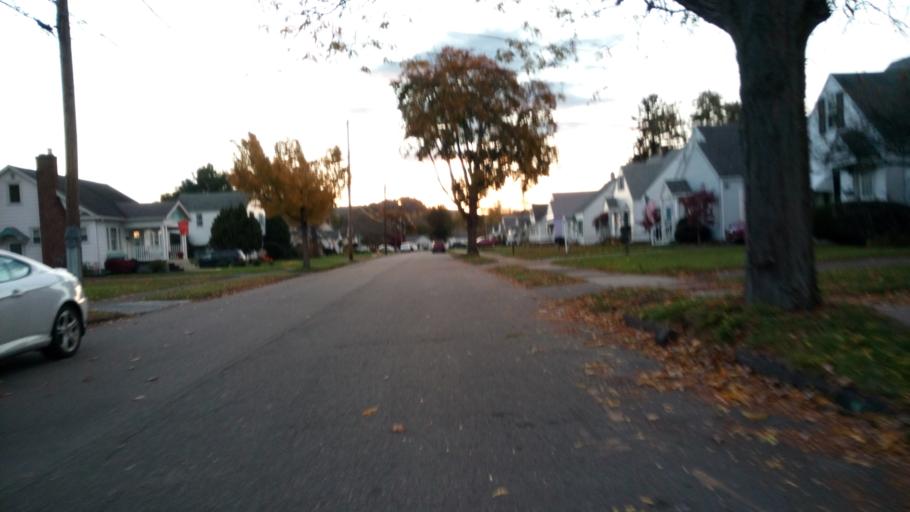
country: US
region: New York
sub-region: Chemung County
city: Elmira
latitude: 42.0778
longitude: -76.8155
